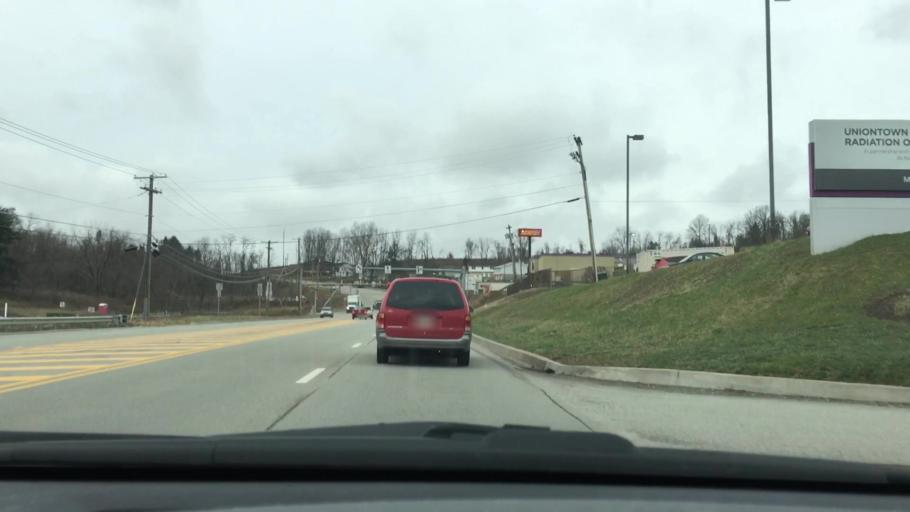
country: US
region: Pennsylvania
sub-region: Fayette County
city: South Uniontown
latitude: 39.9025
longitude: -79.7557
